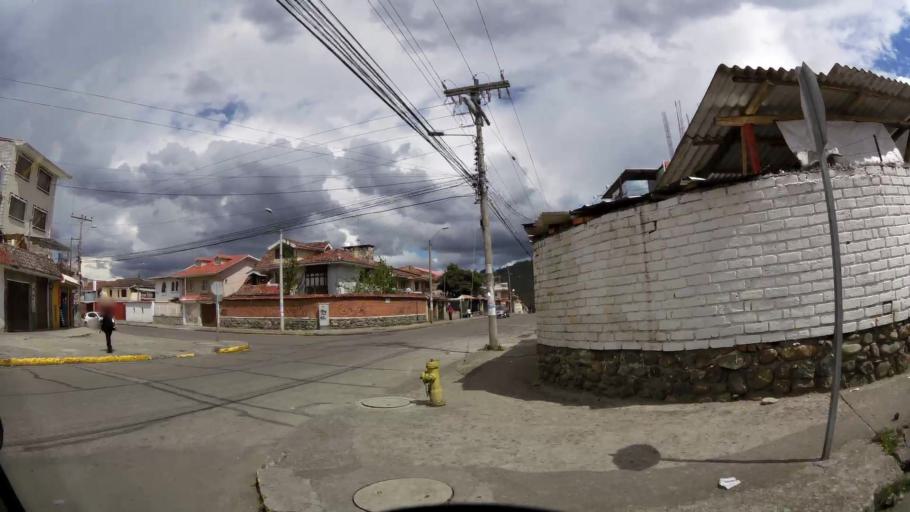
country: EC
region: Azuay
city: Cuenca
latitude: -2.9035
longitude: -78.9942
